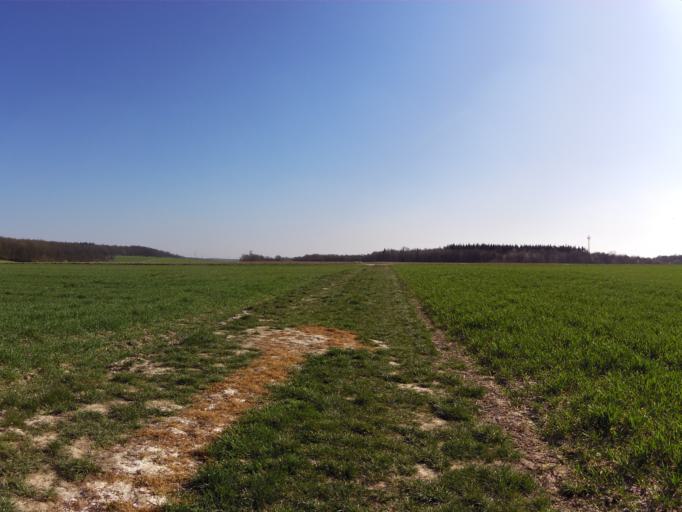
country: DE
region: Bavaria
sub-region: Regierungsbezirk Unterfranken
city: Kurnach
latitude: 49.8348
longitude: 10.0455
